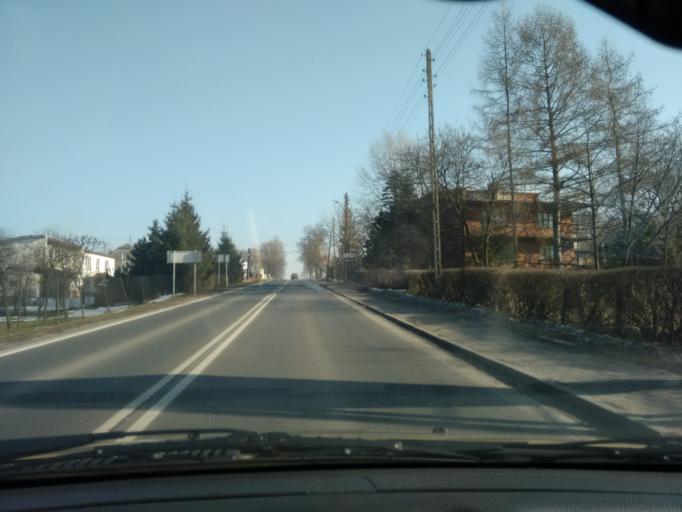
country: PL
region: Lesser Poland Voivodeship
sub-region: Powiat oswiecimski
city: Kety
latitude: 49.8826
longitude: 19.2385
